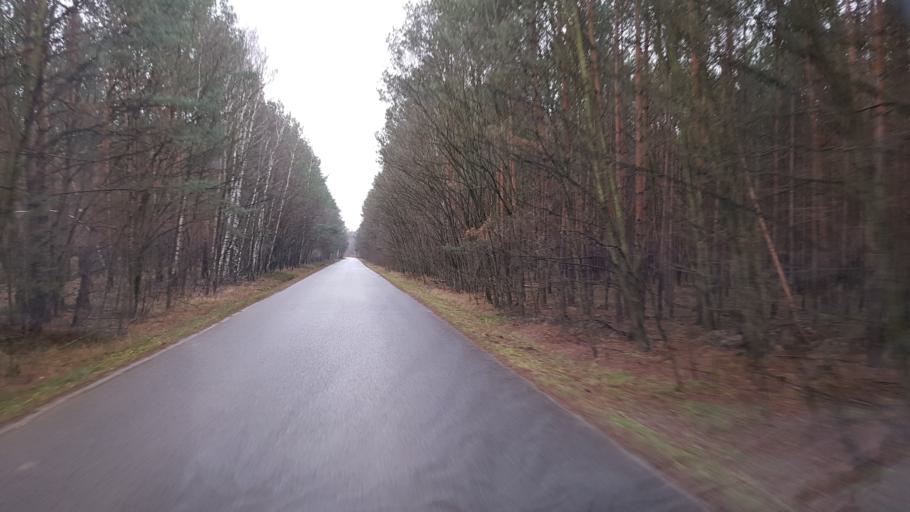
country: DE
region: Brandenburg
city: Calau
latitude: 51.7195
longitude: 14.0003
